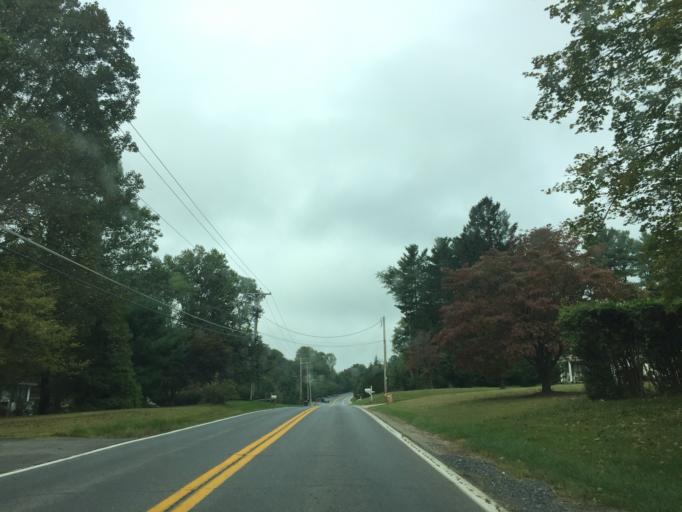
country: US
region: Maryland
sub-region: Baltimore County
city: Owings Mills
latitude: 39.4604
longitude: -76.7402
